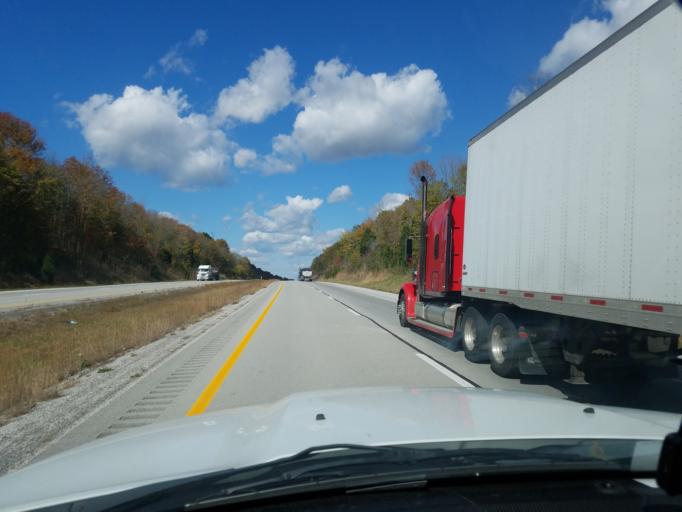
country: US
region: Kentucky
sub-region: Butler County
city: Morgantown
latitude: 37.2549
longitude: -86.7423
